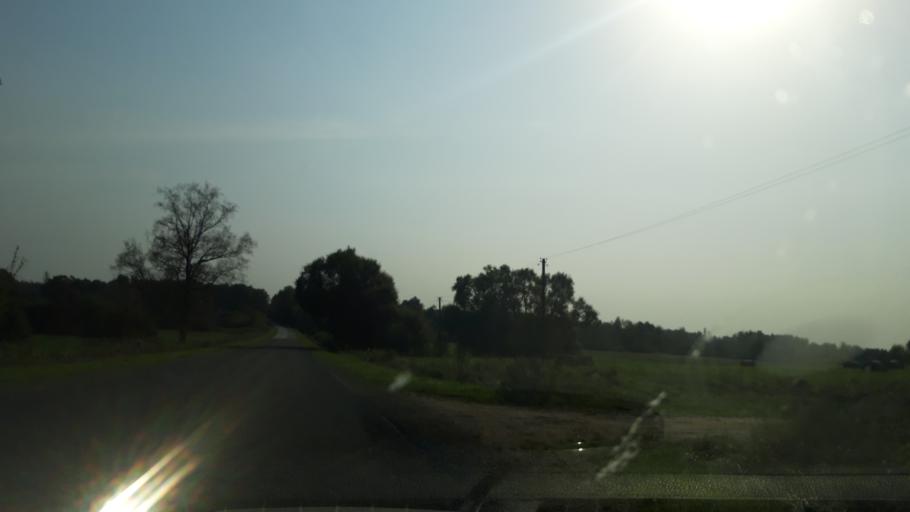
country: LV
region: Burtnieki
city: Matisi
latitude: 57.6579
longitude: 25.2276
